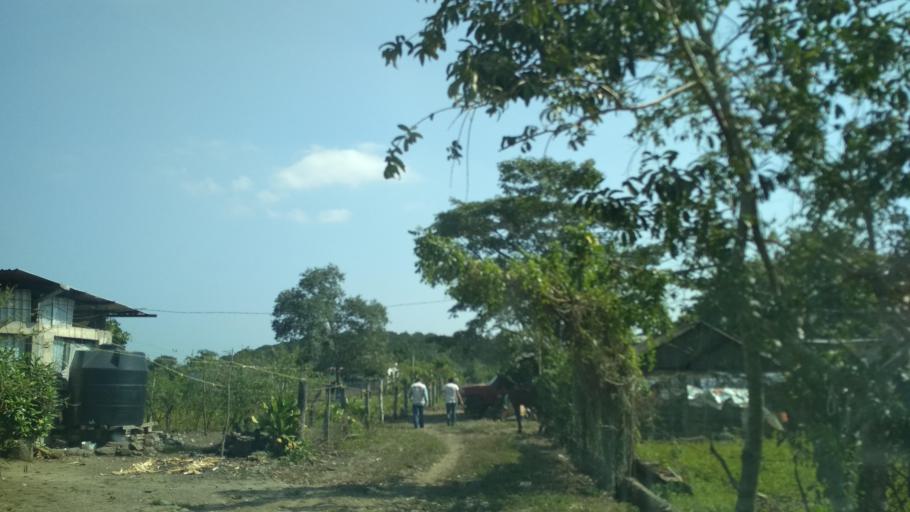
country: MX
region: Puebla
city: San Jose Acateno
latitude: 20.1771
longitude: -97.2305
